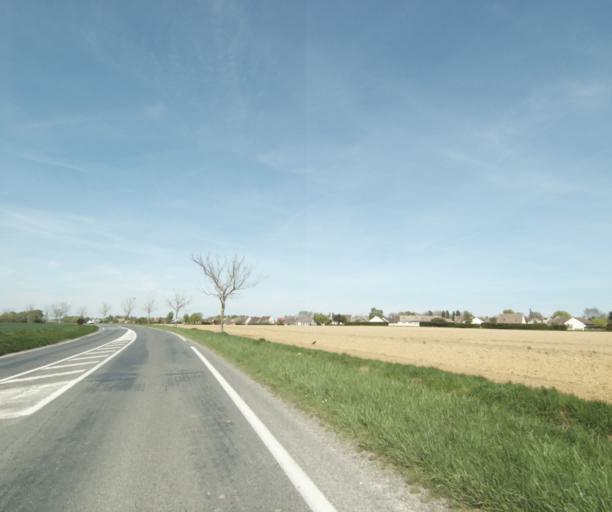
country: FR
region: Ile-de-France
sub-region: Departement de Seine-et-Marne
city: Nangis
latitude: 48.5467
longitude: 3.0152
